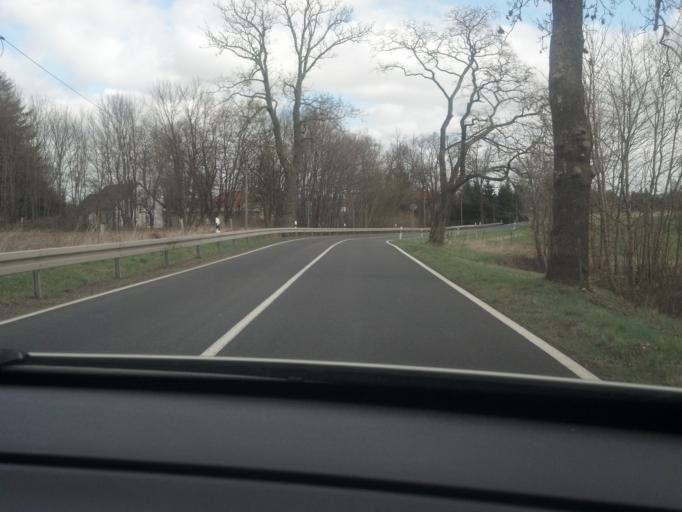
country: DE
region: Brandenburg
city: Gerdshagen
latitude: 53.3059
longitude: 12.2292
